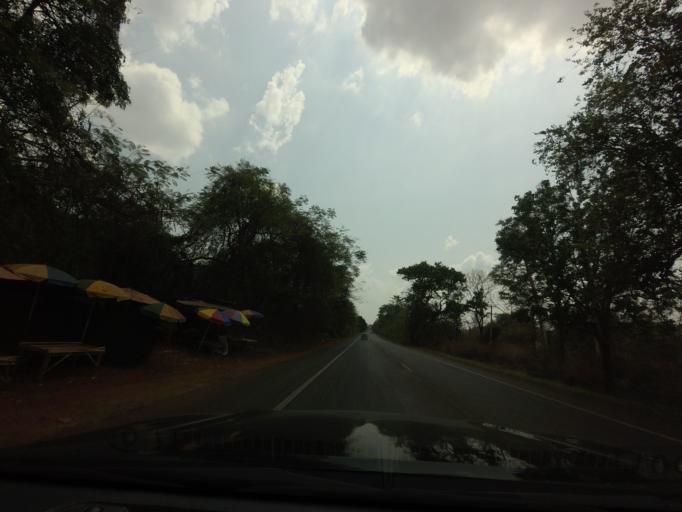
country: TH
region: Kanchanaburi
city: Sai Yok
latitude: 14.1486
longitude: 99.1440
